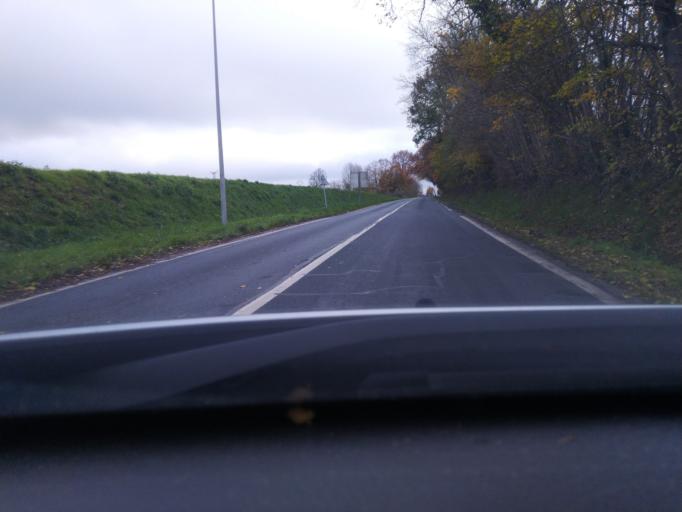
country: FR
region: Haute-Normandie
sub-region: Departement de la Seine-Maritime
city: La Vaupaliere
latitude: 49.4978
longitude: 0.9841
